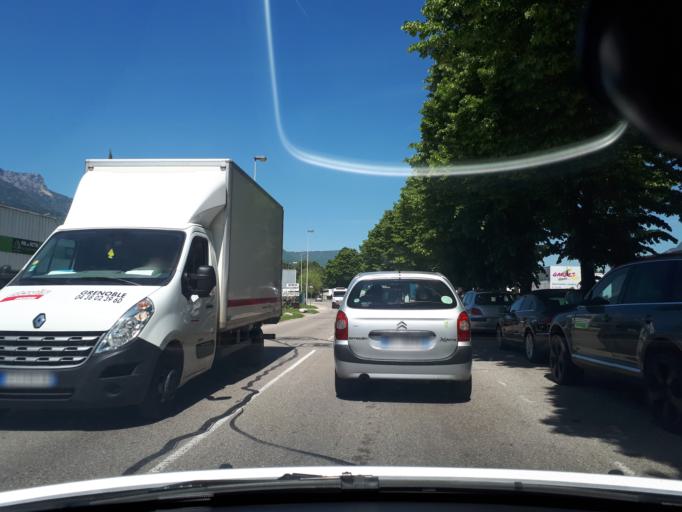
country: FR
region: Rhone-Alpes
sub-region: Departement de l'Isere
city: Saint-Egreve
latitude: 45.2225
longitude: 5.6755
